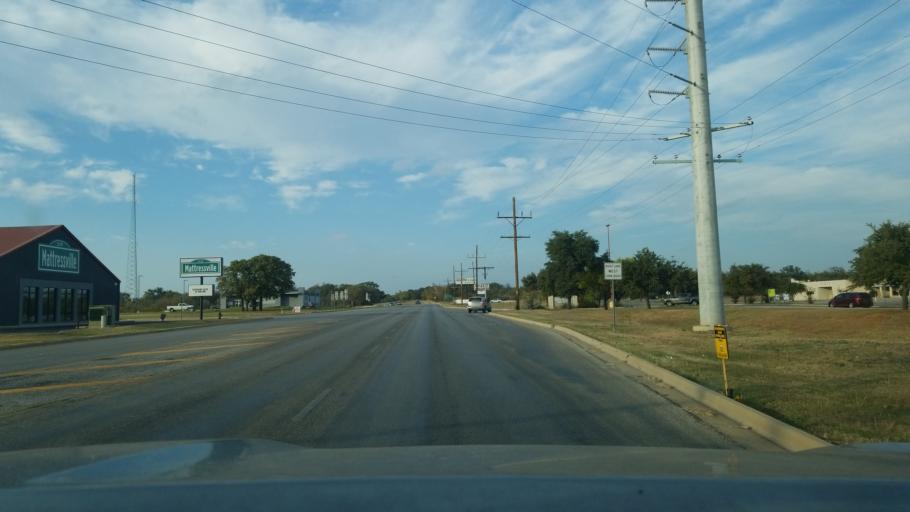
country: US
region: Texas
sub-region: Brown County
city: Early
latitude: 31.7369
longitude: -98.9631
